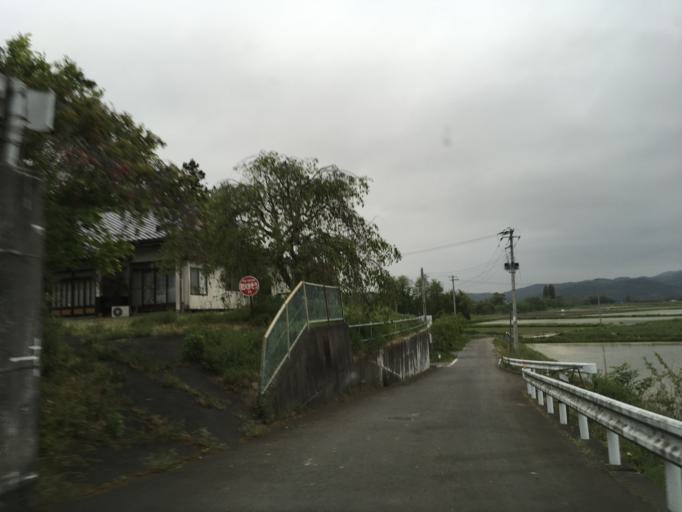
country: JP
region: Miyagi
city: Wakuya
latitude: 38.7094
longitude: 141.2842
